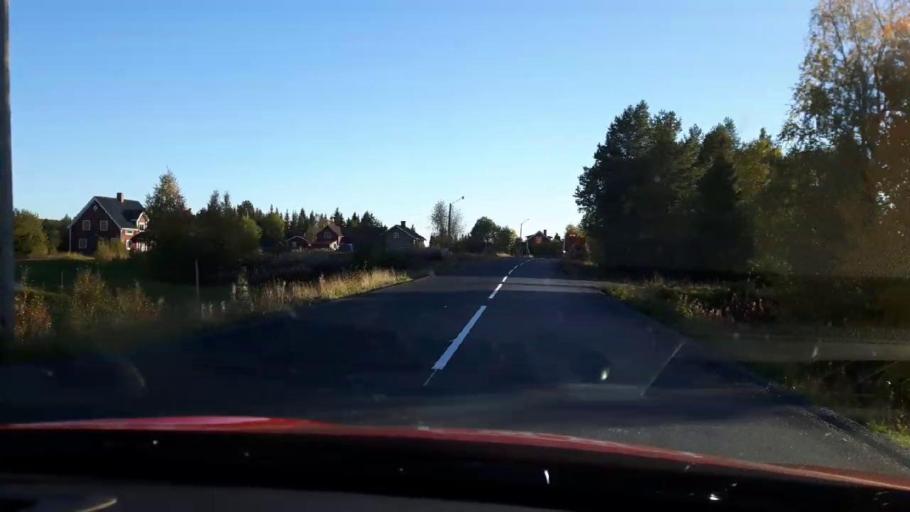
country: SE
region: Jaemtland
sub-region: OEstersunds Kommun
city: Lit
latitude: 63.5644
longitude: 14.9174
